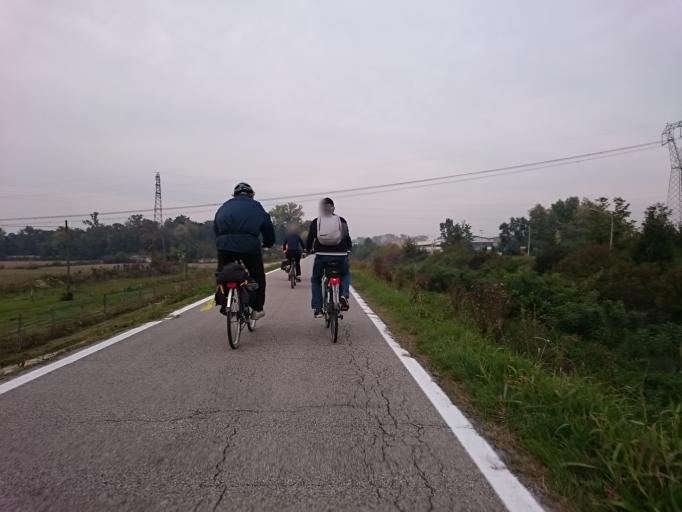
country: IT
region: Veneto
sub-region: Provincia di Padova
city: Mandriola-Sant'Agostino
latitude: 45.3591
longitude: 11.8380
